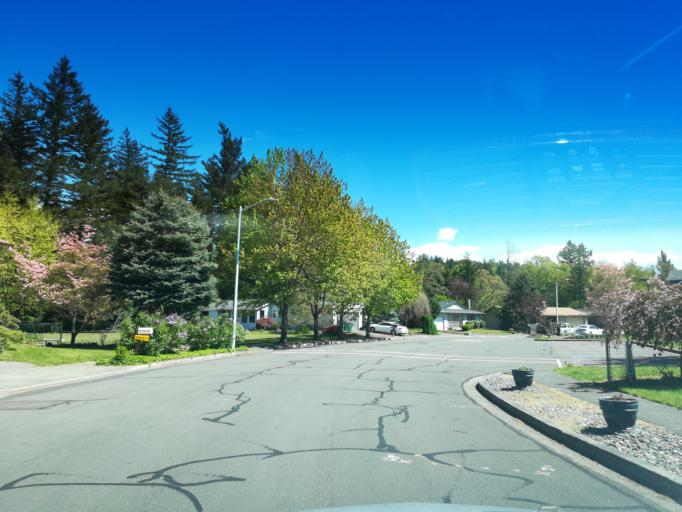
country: US
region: Oregon
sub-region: Multnomah County
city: Troutdale
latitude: 45.5292
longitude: -122.3757
